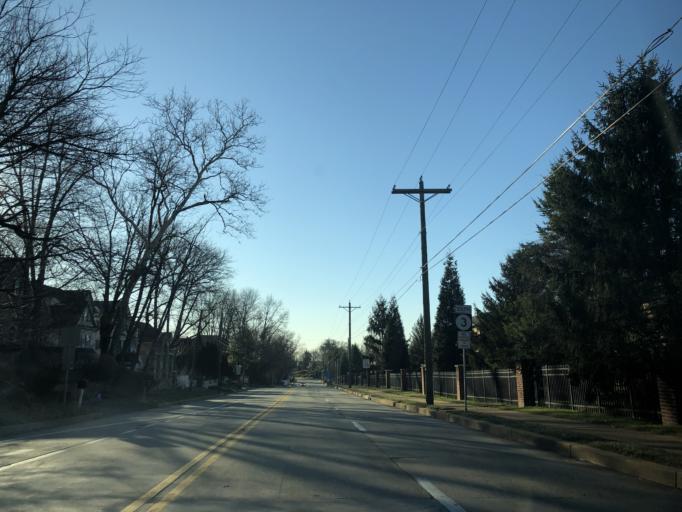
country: US
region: Delaware
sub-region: New Castle County
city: Bellefonte
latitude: 39.7600
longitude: -75.5111
